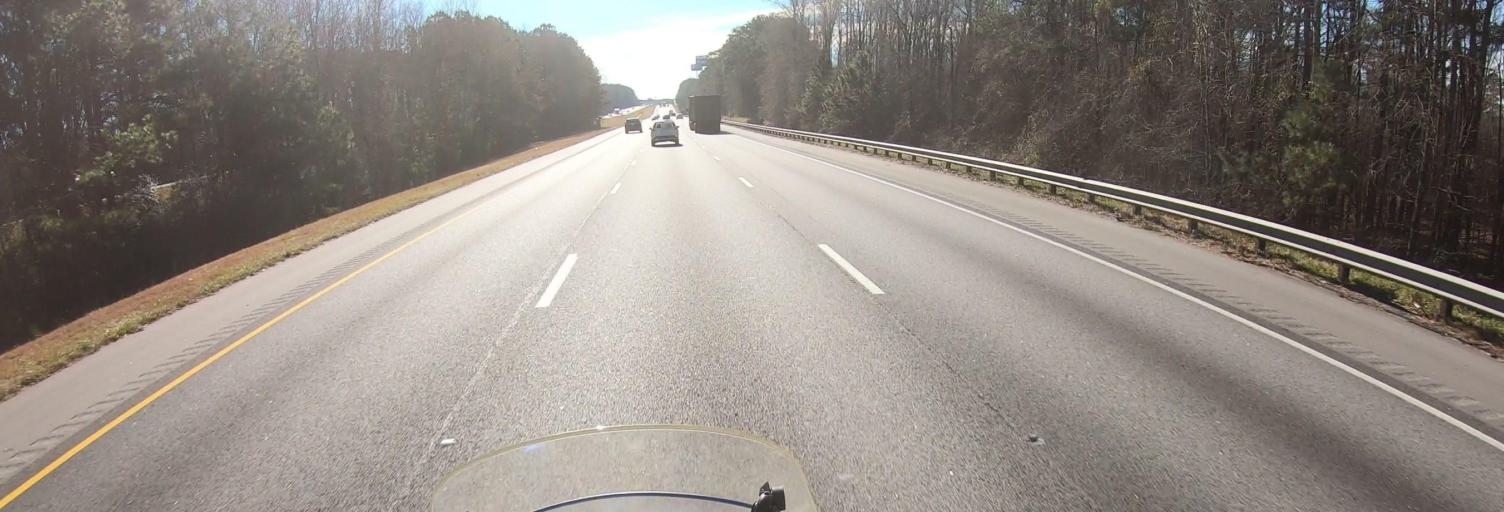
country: US
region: Georgia
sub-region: Henry County
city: Locust Grove
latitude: 33.3847
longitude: -84.1457
